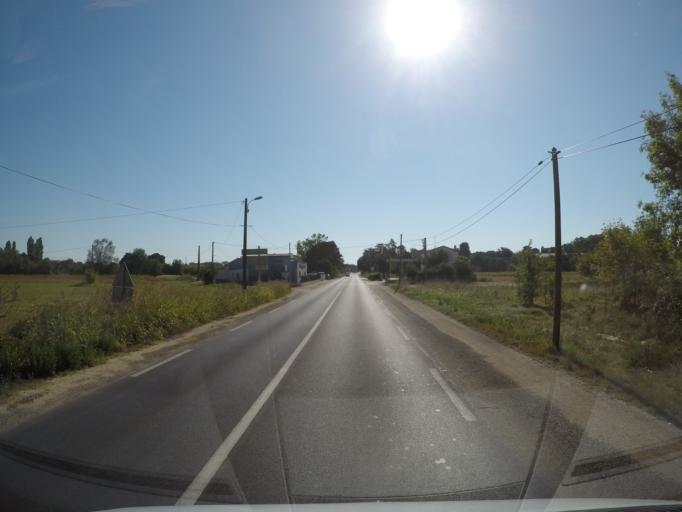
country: FR
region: Languedoc-Roussillon
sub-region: Departement du Gard
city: Moussac
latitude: 43.9769
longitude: 4.2105
